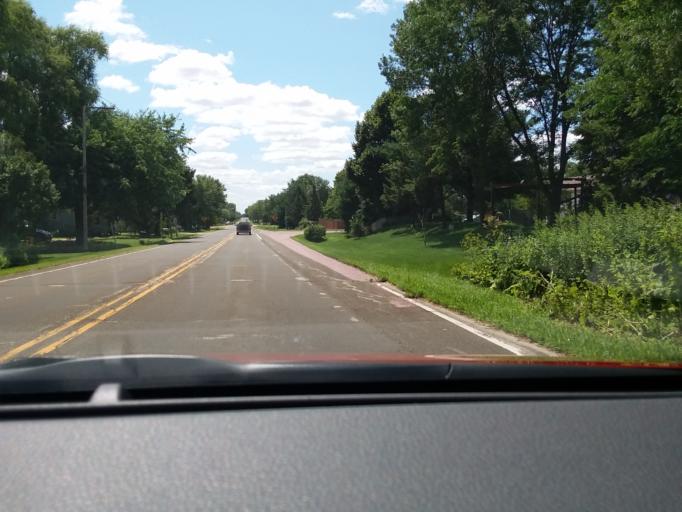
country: US
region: Wisconsin
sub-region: Dane County
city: Windsor
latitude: 43.2191
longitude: -89.3434
